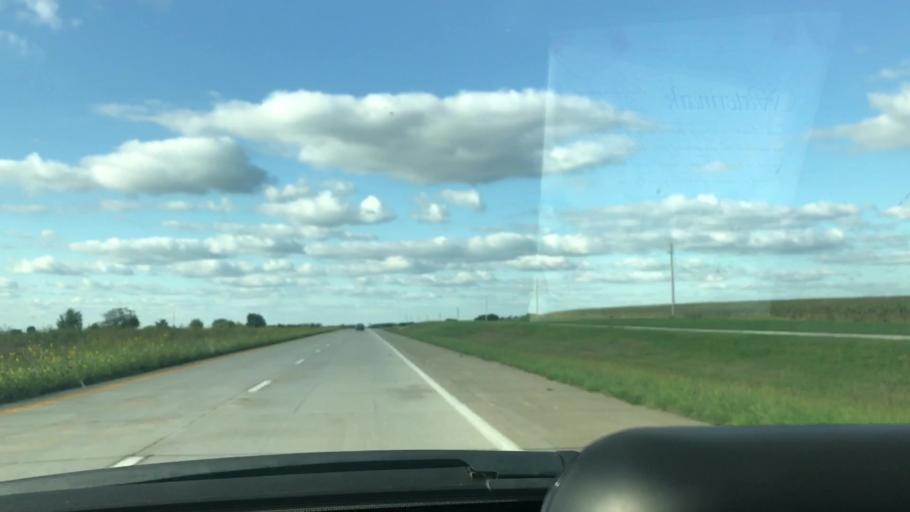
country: US
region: Missouri
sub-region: Benton County
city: Cole Camp
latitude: 38.5061
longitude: -93.2729
